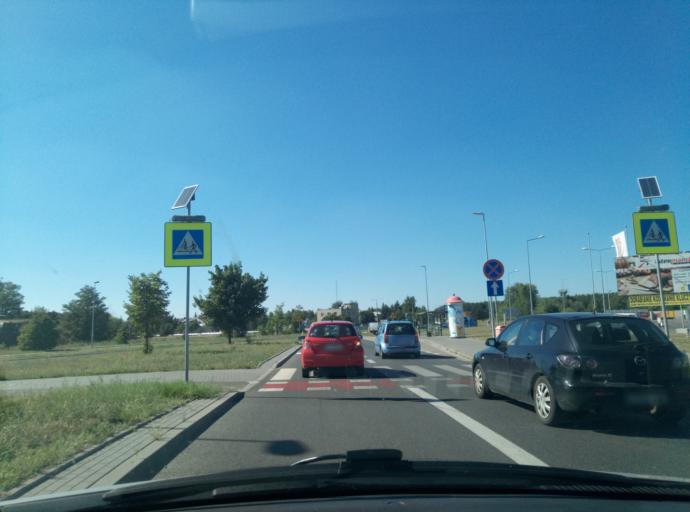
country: PL
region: Kujawsko-Pomorskie
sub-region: Torun
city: Torun
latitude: 53.0409
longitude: 18.5982
